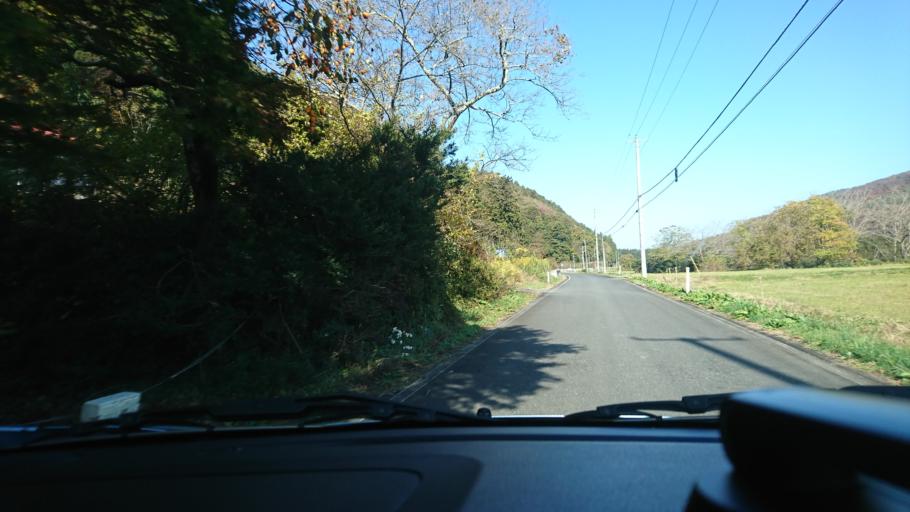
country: JP
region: Iwate
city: Ichinoseki
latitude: 38.8090
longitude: 141.2471
